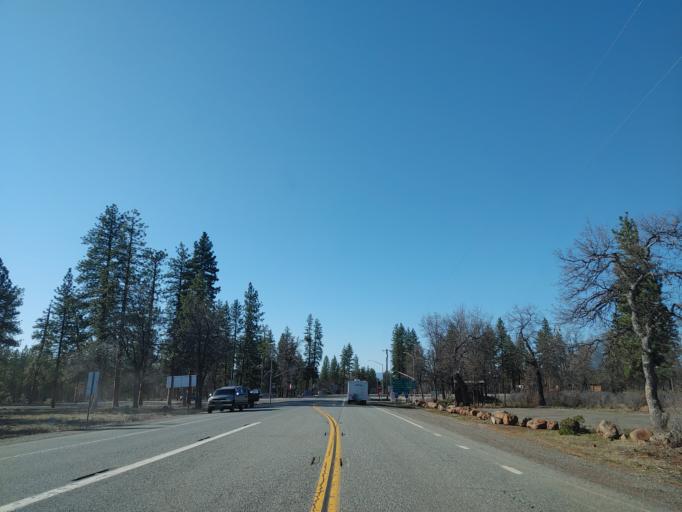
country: US
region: California
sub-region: Shasta County
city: Burney
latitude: 40.9370
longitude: -121.6059
